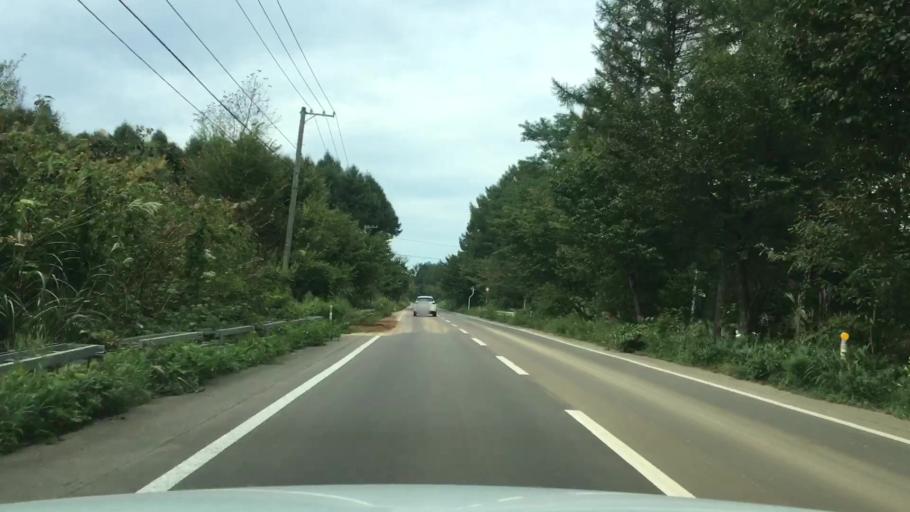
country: JP
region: Aomori
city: Shimokizukuri
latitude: 40.7069
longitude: 140.3415
